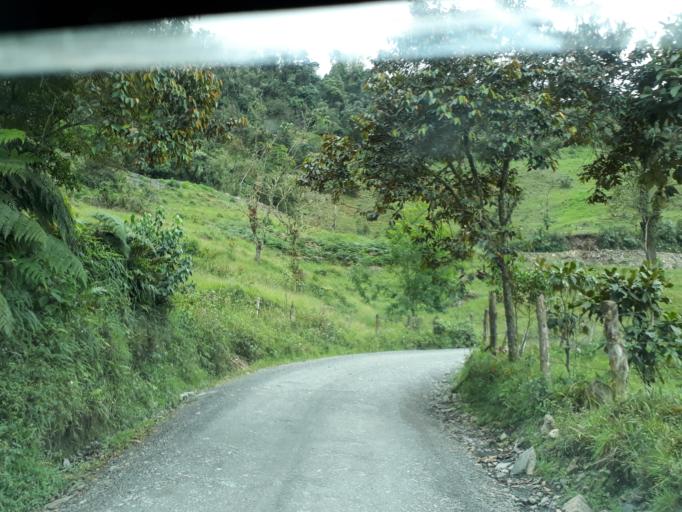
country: CO
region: Cundinamarca
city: Pacho
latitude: 5.2595
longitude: -74.1823
